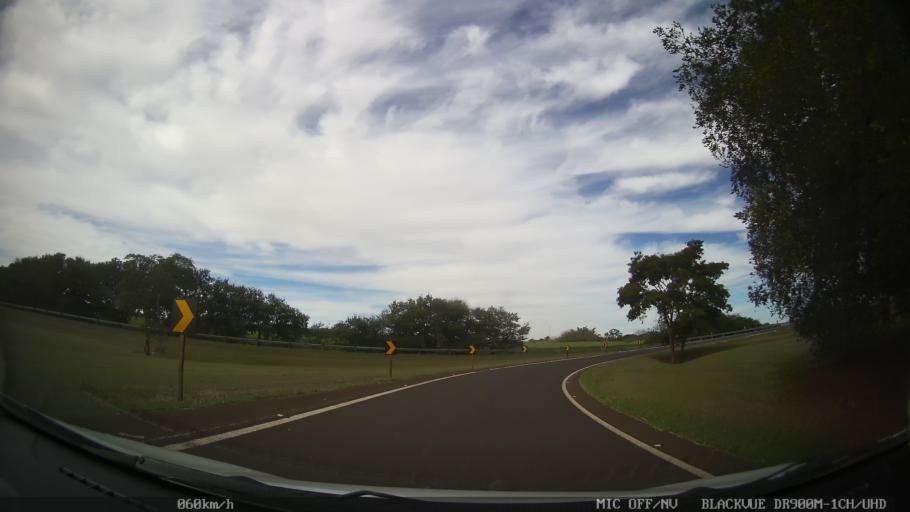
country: BR
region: Sao Paulo
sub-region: Taquaritinga
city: Taquaritinga
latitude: -21.4754
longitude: -48.5965
